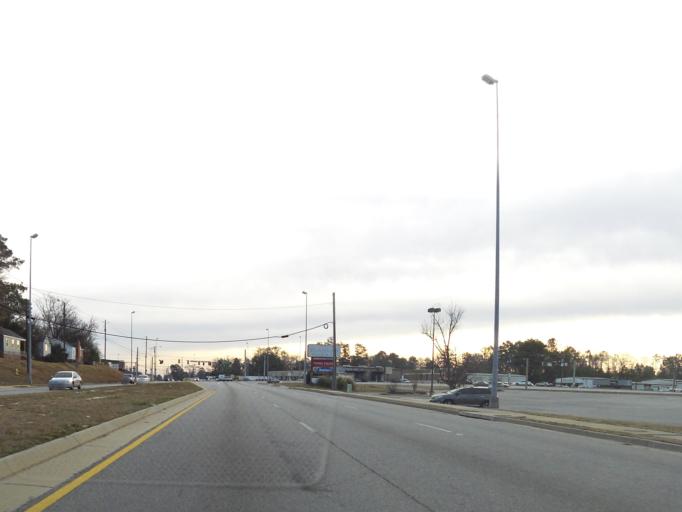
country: US
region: Georgia
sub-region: Bibb County
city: Macon
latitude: 32.8264
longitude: -83.7155
